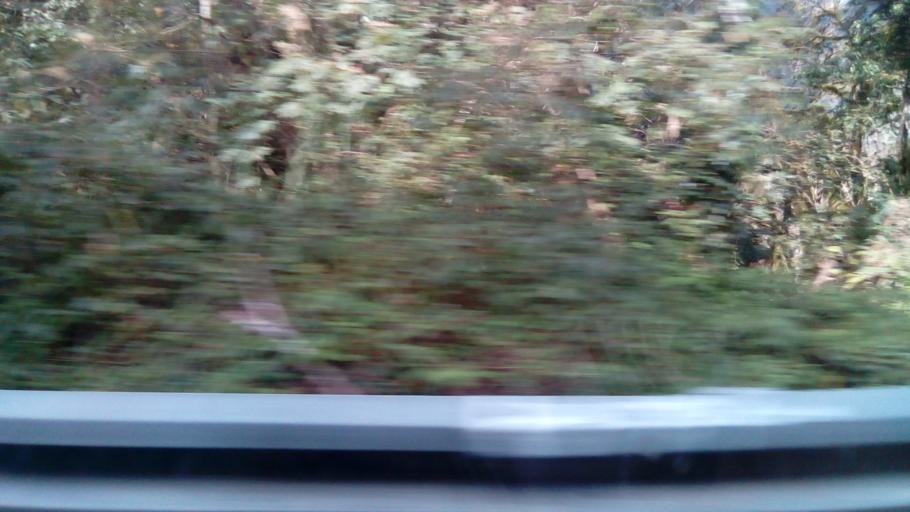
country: TW
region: Taiwan
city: Daxi
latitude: 24.4052
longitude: 121.3623
